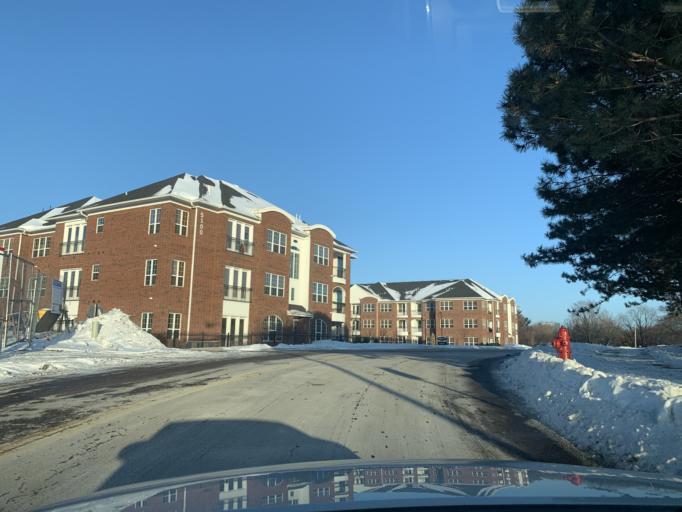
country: US
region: Minnesota
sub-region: Hennepin County
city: Edina
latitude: 44.8546
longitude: -93.3468
